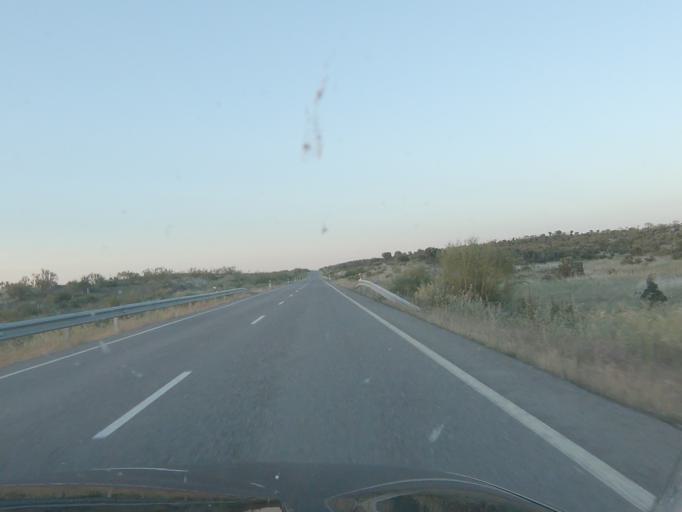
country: ES
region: Extremadura
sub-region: Provincia de Caceres
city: Salorino
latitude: 39.5971
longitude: -6.9844
